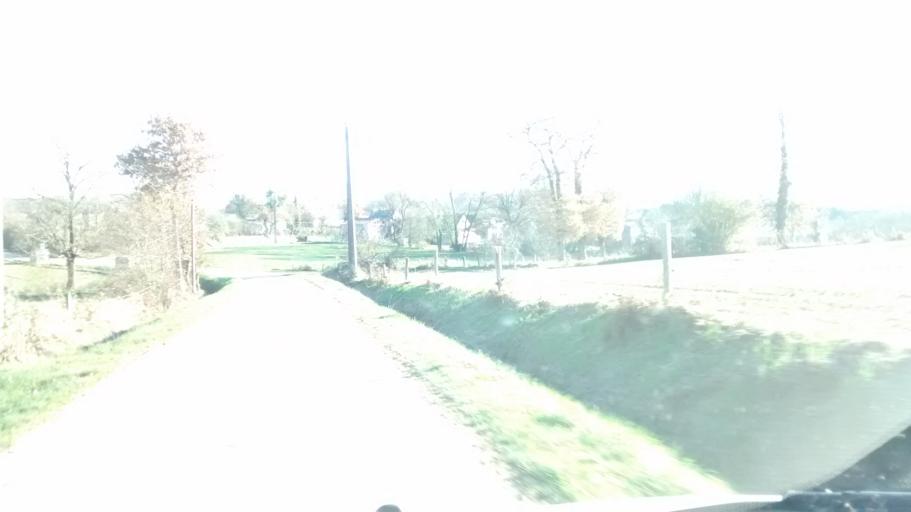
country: FR
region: Brittany
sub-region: Departement d'Ille-et-Vilaine
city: La Bouexiere
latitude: 48.2064
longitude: -1.4627
